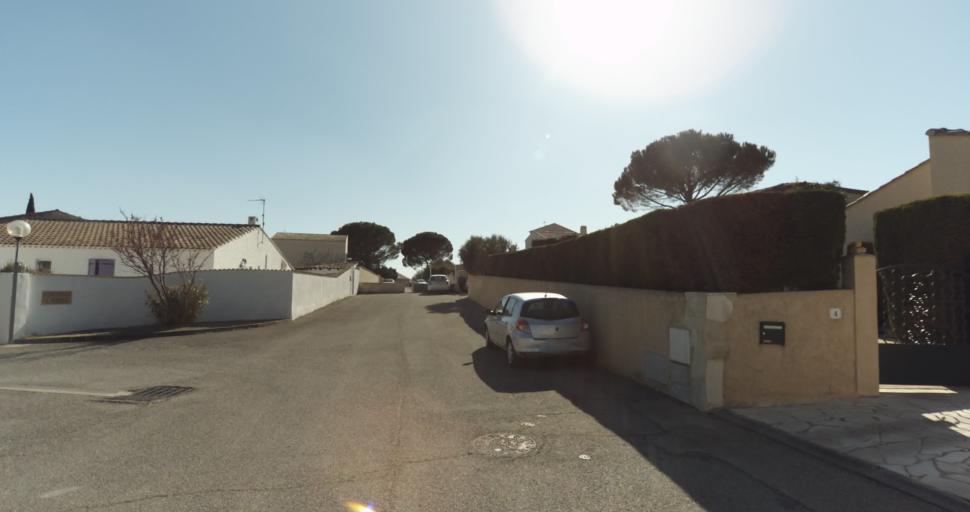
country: FR
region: Provence-Alpes-Cote d'Azur
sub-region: Departement des Bouches-du-Rhone
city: Pelissanne
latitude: 43.6354
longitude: 5.1399
